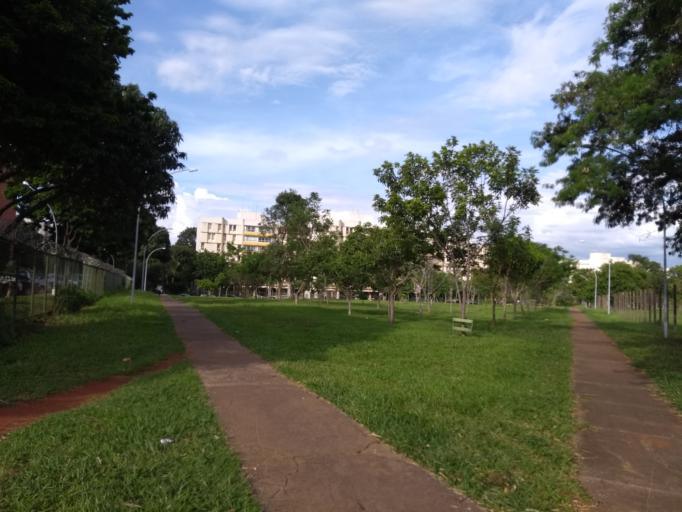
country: BR
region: Federal District
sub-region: Brasilia
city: Brasilia
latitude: -15.8076
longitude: -47.9420
